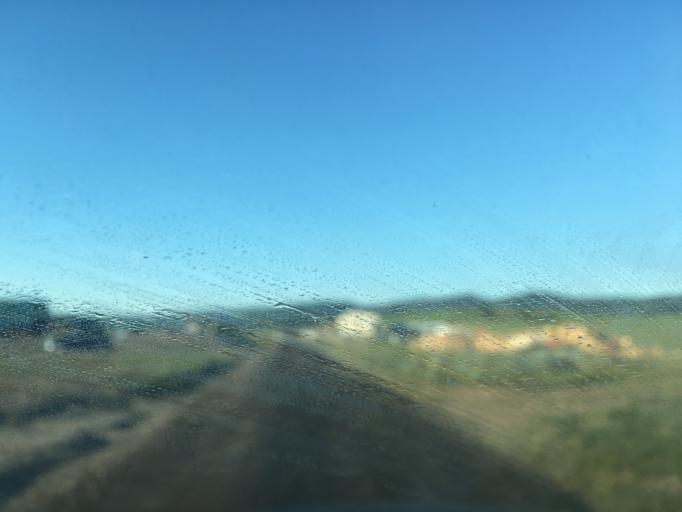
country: US
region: Montana
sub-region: Gallatin County
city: West Yellowstone
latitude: 44.7011
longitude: -111.2124
